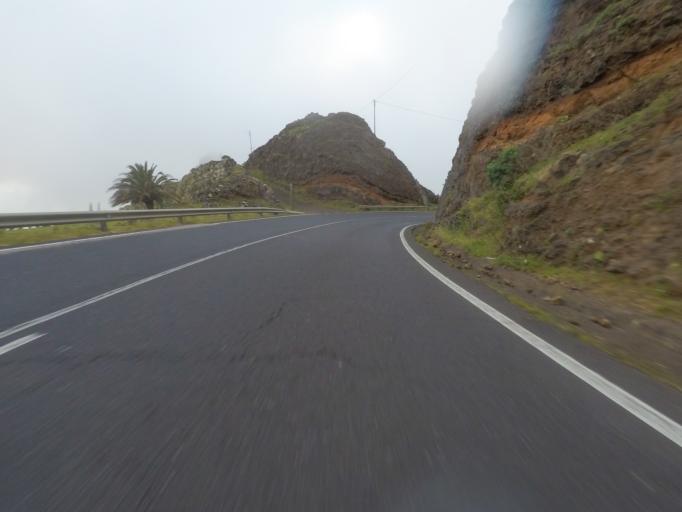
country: ES
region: Canary Islands
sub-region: Provincia de Santa Cruz de Tenerife
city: Alajero
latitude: 28.0948
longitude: -17.1901
